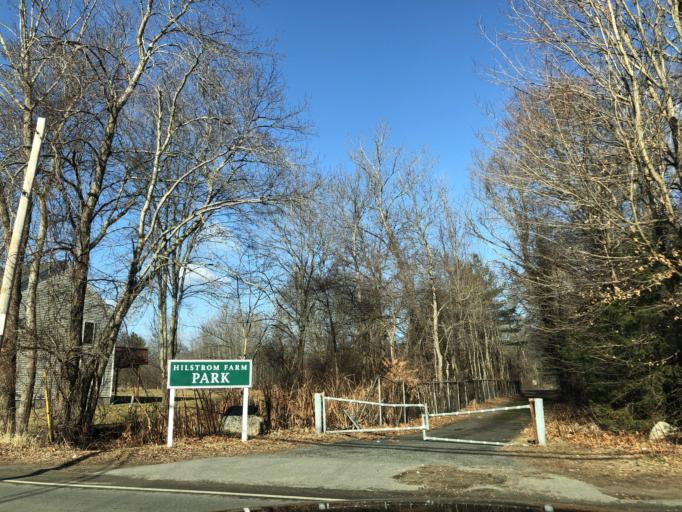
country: US
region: Massachusetts
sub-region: Plymouth County
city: Brockton
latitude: 42.1072
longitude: -71.0003
